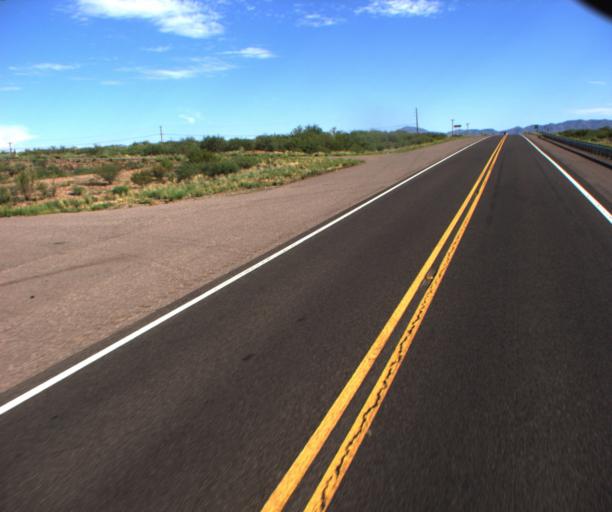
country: US
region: Arizona
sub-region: Greenlee County
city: Clifton
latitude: 32.9400
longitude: -109.2345
